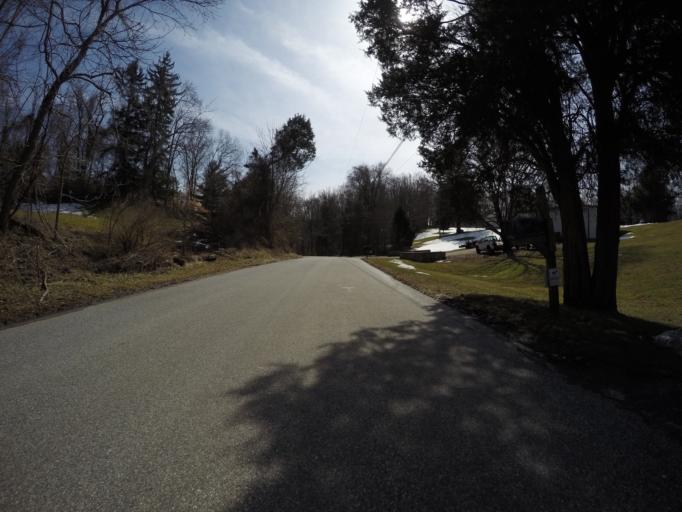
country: US
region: Maryland
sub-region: Baltimore County
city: Hunt Valley
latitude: 39.5197
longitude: -76.6572
